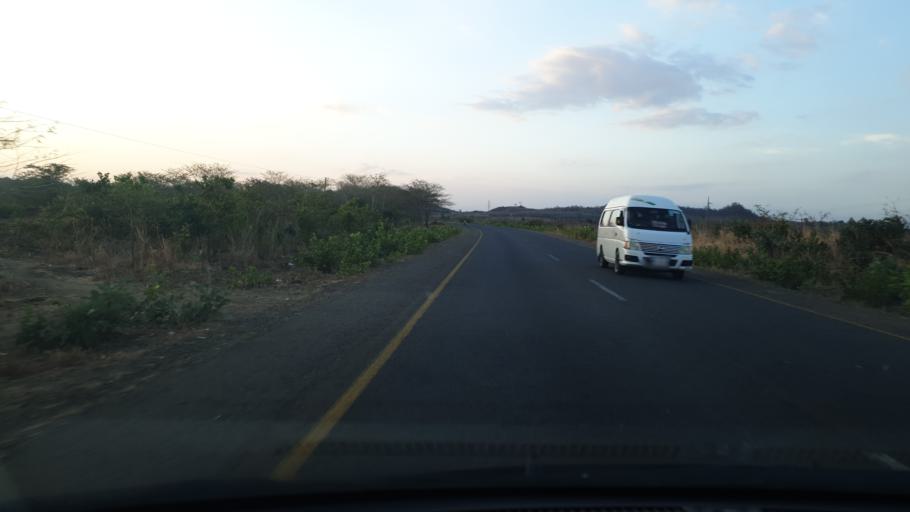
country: MW
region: Central Region
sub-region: Salima District
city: Salima
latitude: -13.7535
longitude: 34.3296
